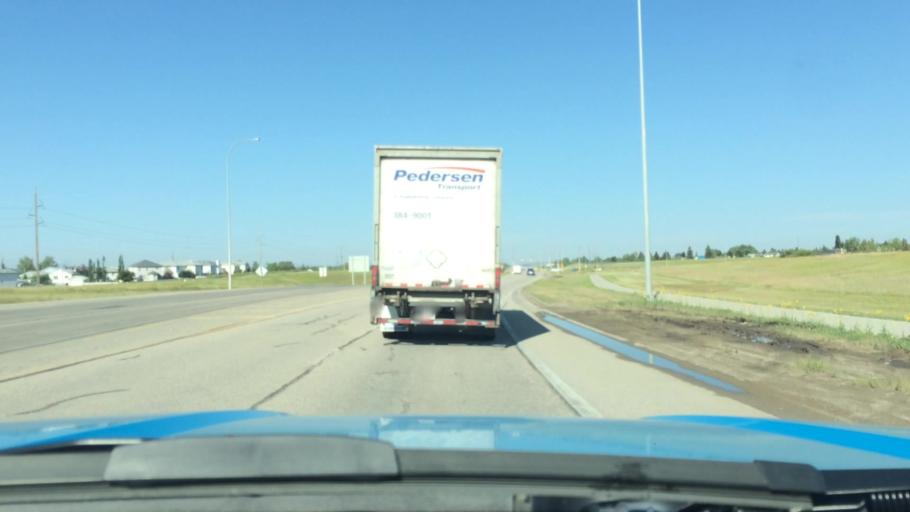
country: CA
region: Alberta
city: Chestermere
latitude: 51.0962
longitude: -113.9286
